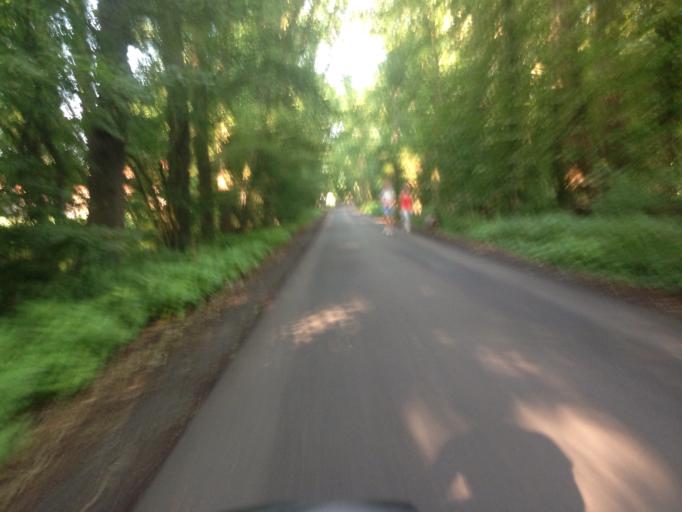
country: DE
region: North Rhine-Westphalia
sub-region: Regierungsbezirk Munster
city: Muenster
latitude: 51.9875
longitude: 7.5972
